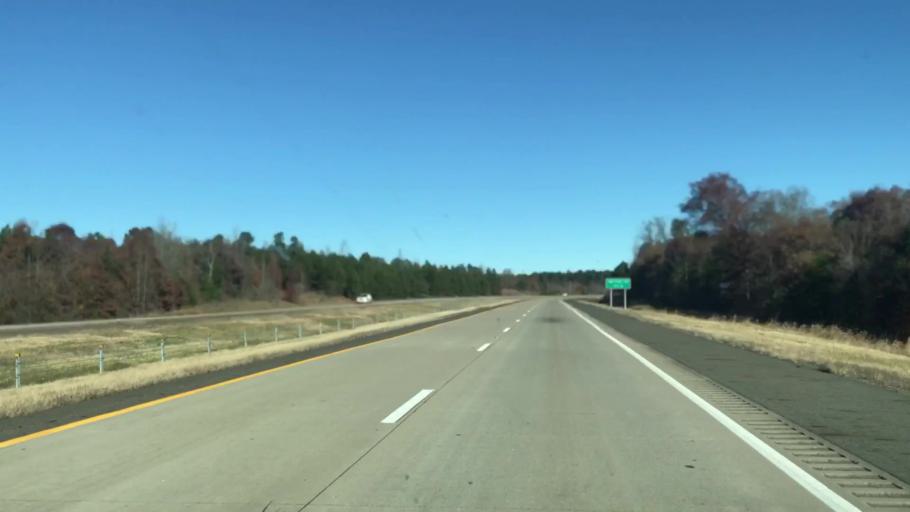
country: US
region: Louisiana
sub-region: Caddo Parish
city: Vivian
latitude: 33.1030
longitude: -93.8956
